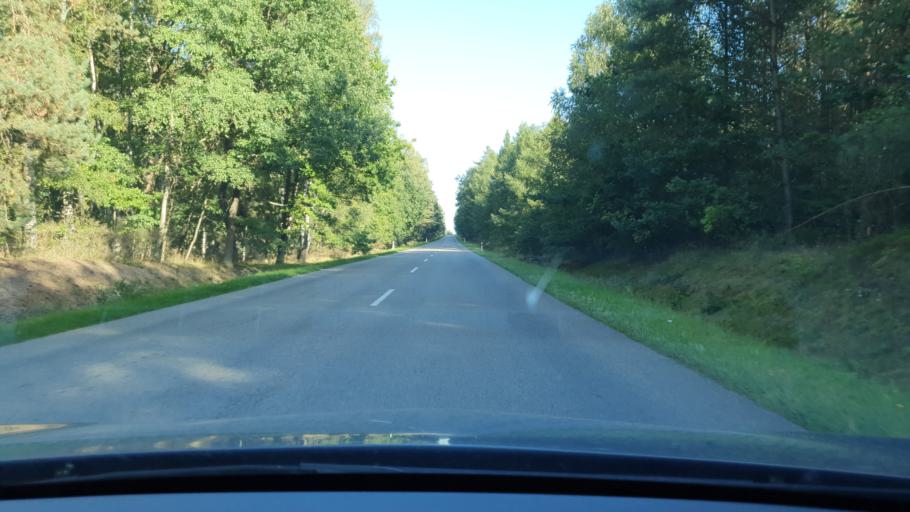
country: PL
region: West Pomeranian Voivodeship
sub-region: Powiat kamienski
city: Golczewo
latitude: 53.8132
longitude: 15.0875
